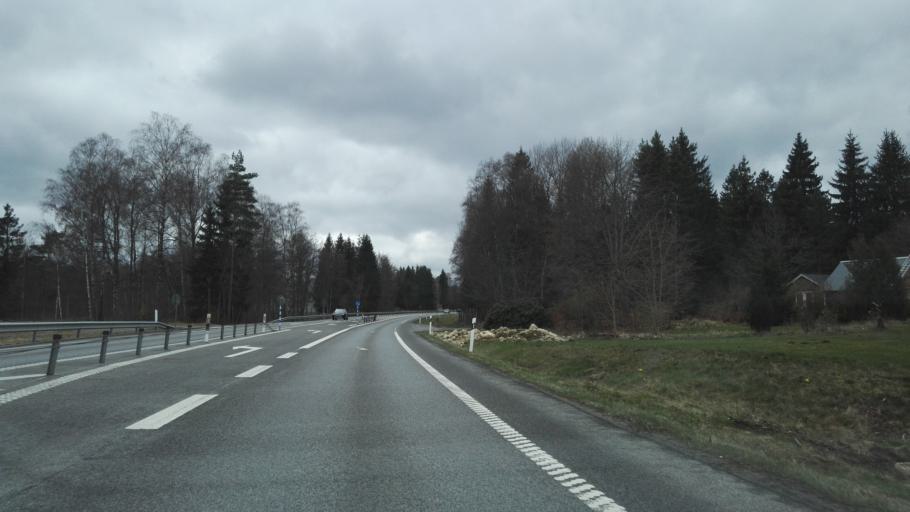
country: SE
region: Kronoberg
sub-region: Alvesta Kommun
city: Vislanda
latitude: 56.7163
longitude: 14.4522
